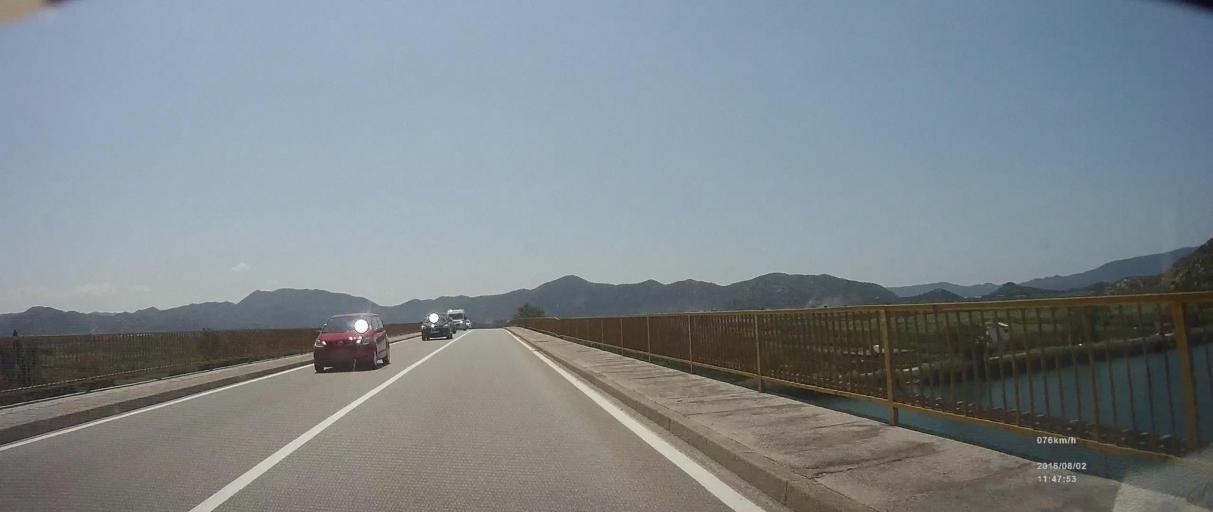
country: HR
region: Dubrovacko-Neretvanska
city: Komin
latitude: 43.0388
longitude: 17.4848
